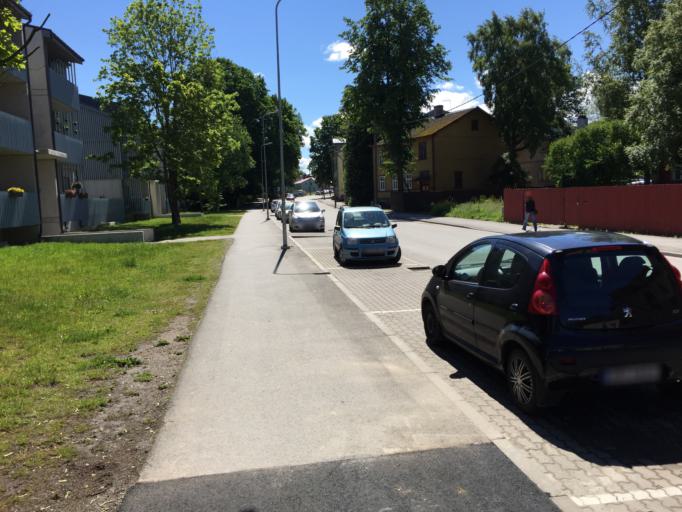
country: EE
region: Harju
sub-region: Tallinna linn
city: Tallinn
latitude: 59.4489
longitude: 24.7336
